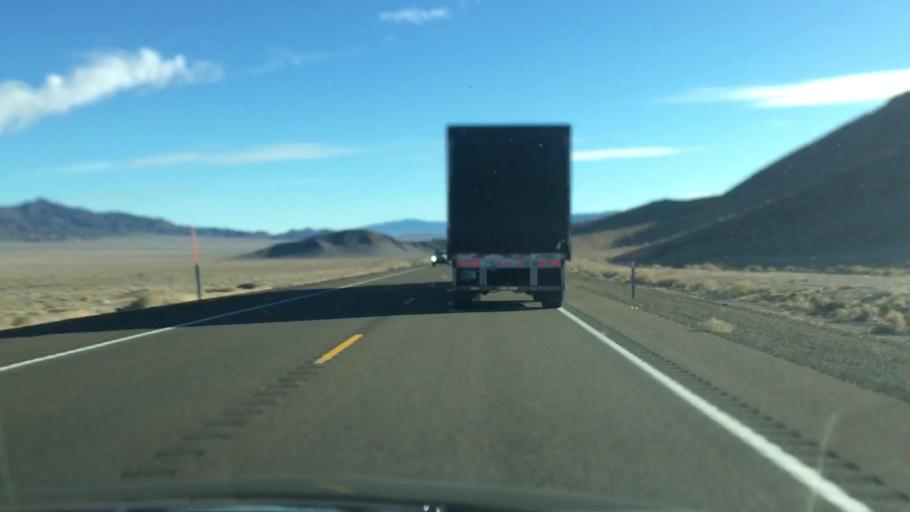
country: US
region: Nevada
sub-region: Nye County
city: Tonopah
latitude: 38.1678
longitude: -117.9551
